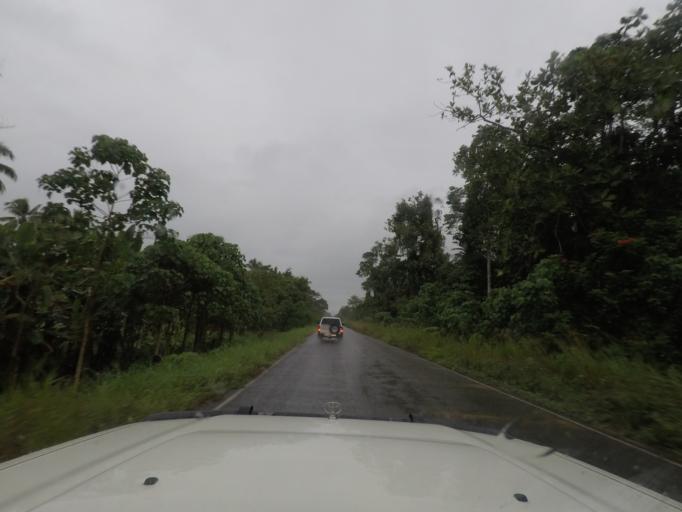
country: PG
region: Madang
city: Madang
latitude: -5.3434
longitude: 145.7097
